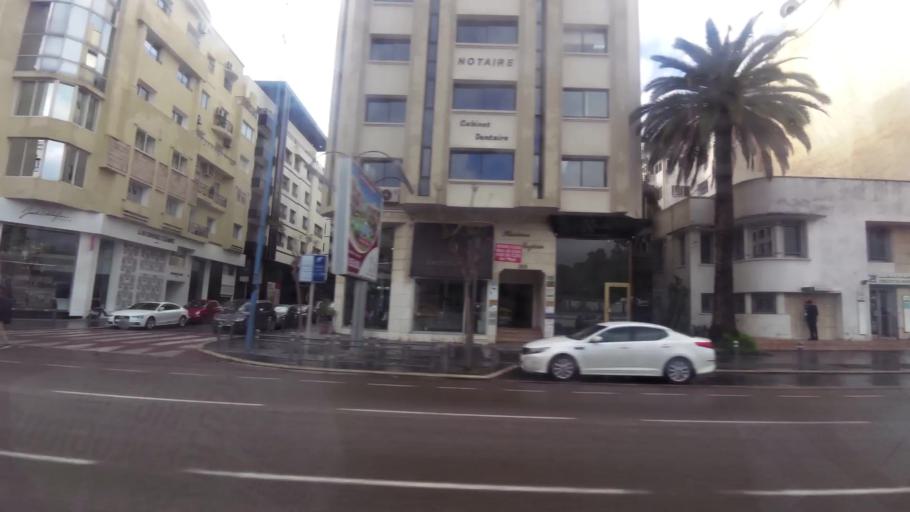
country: MA
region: Grand Casablanca
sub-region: Casablanca
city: Casablanca
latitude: 33.5890
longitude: -7.6412
